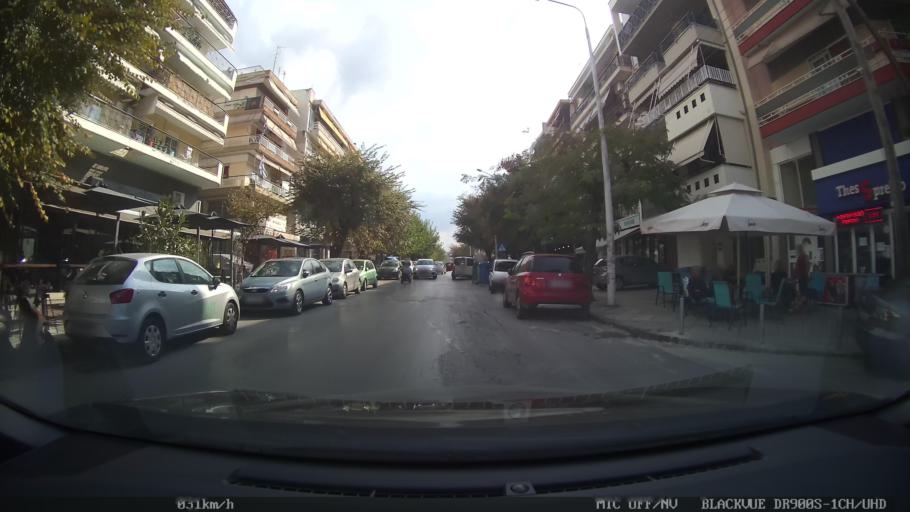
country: GR
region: Central Macedonia
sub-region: Nomos Thessalonikis
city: Triandria
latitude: 40.6126
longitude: 22.9729
